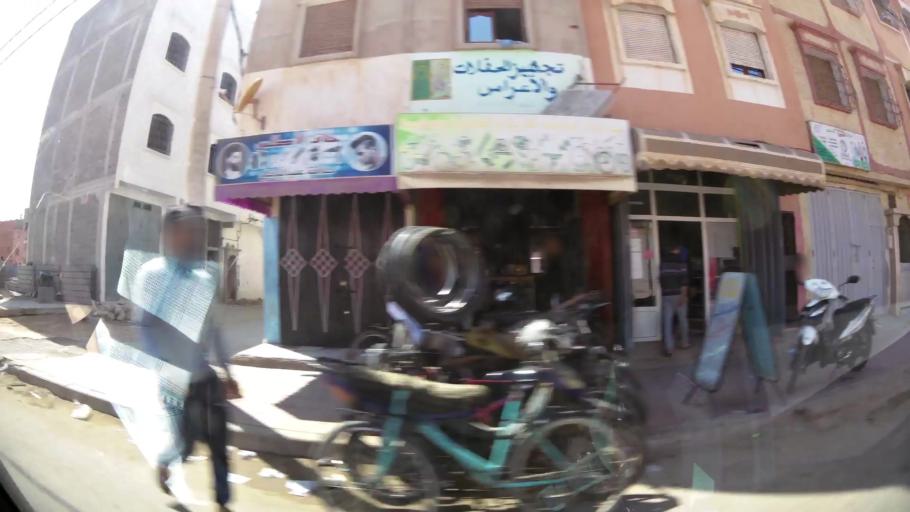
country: MA
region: Souss-Massa-Draa
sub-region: Inezgane-Ait Mellou
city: Inezgane
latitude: 30.3469
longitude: -9.5426
